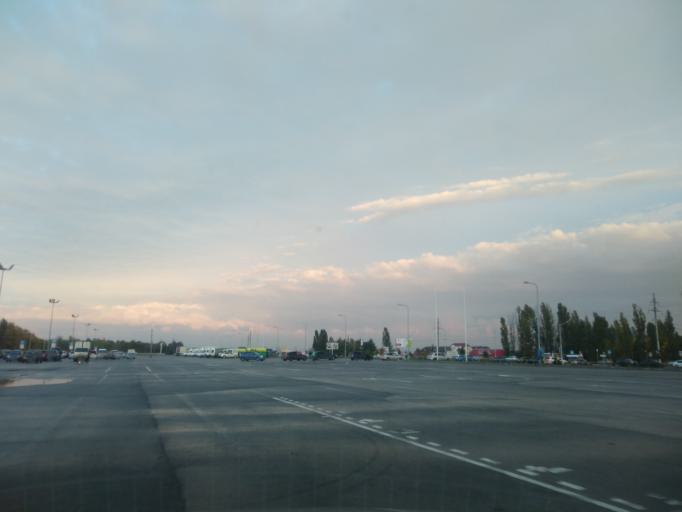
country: RU
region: Lipetsk
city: Syrskoye
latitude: 52.5733
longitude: 39.5220
